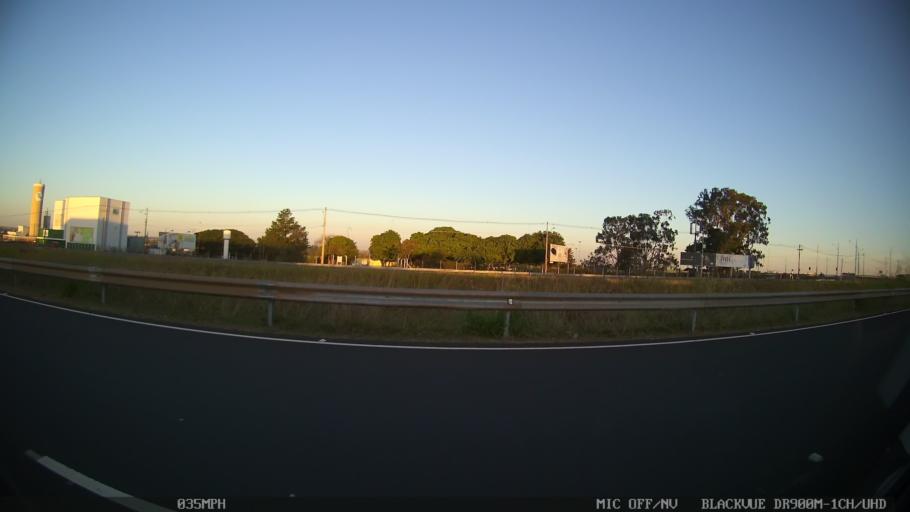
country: BR
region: Sao Paulo
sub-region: Sao Jose Do Rio Preto
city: Sao Jose do Rio Preto
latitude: -20.8647
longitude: -49.4122
